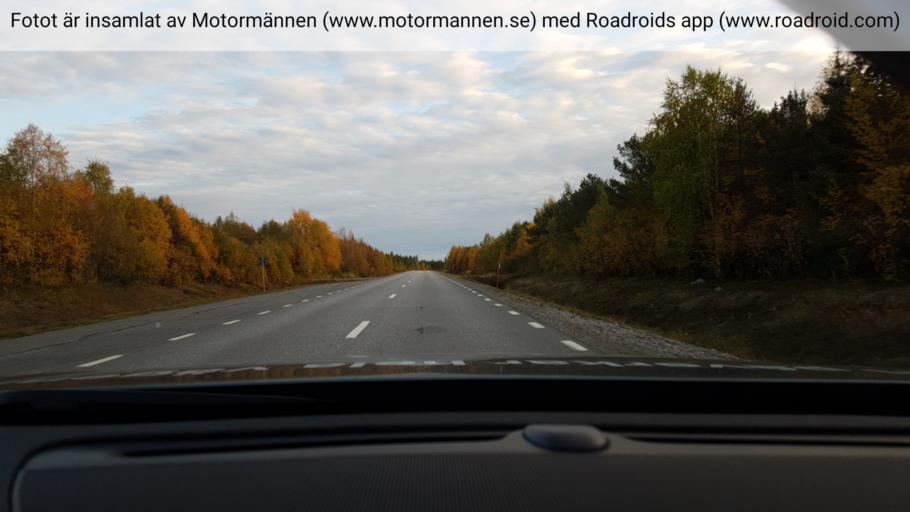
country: SE
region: Norrbotten
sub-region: Jokkmokks Kommun
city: Jokkmokk
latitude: 66.4205
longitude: 19.6854
